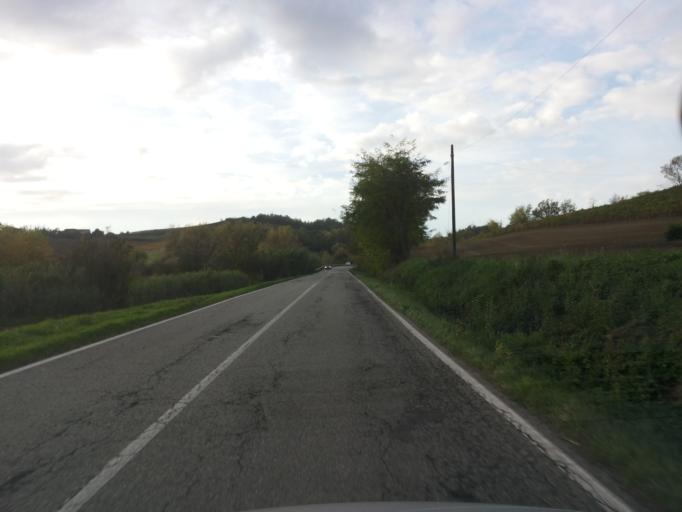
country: IT
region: Piedmont
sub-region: Provincia di Alessandria
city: San Giorgio
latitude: 45.1032
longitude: 8.3994
